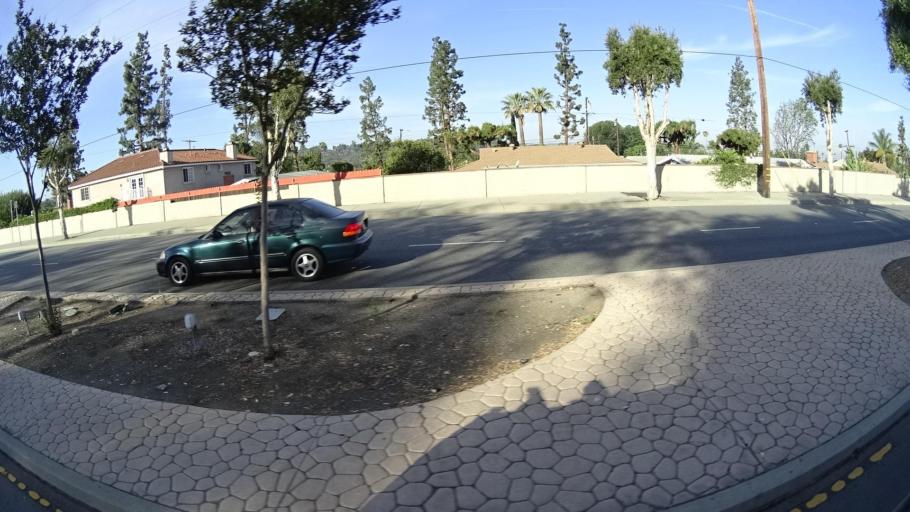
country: US
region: California
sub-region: Los Angeles County
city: South San Jose Hills
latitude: 34.0327
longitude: -117.9160
